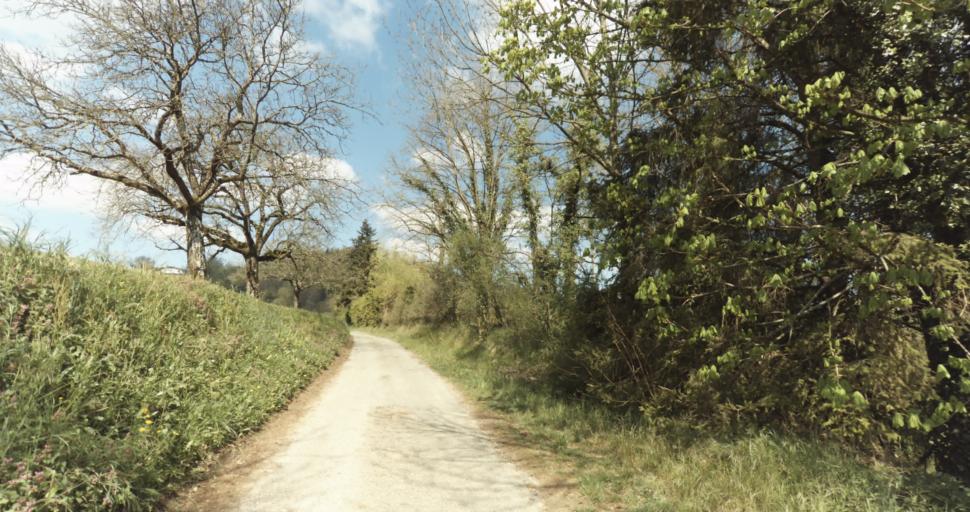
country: FR
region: Rhone-Alpes
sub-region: Departement de l'Isere
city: Saint-Verand
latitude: 45.1638
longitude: 5.3288
